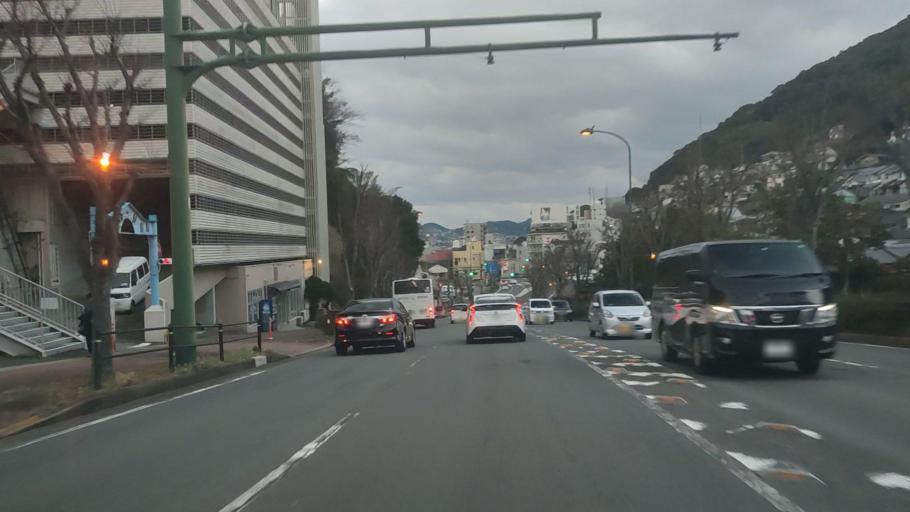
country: JP
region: Nagasaki
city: Nagasaki-shi
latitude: 32.7654
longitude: 129.8901
